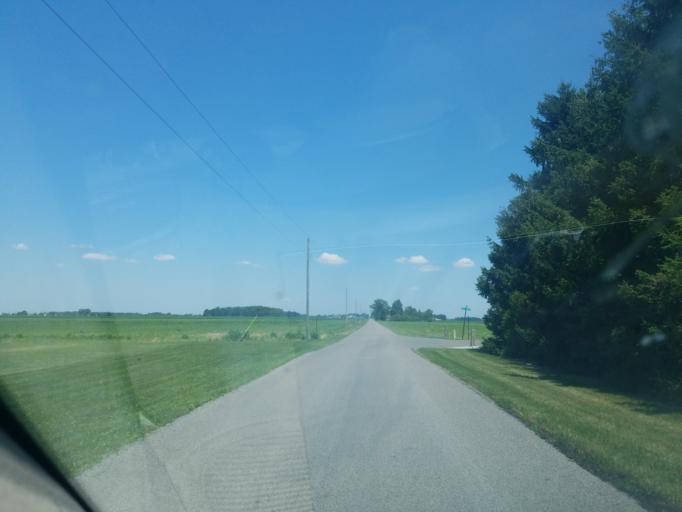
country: US
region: Ohio
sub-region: Allen County
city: Spencerville
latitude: 40.7645
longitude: -84.3496
